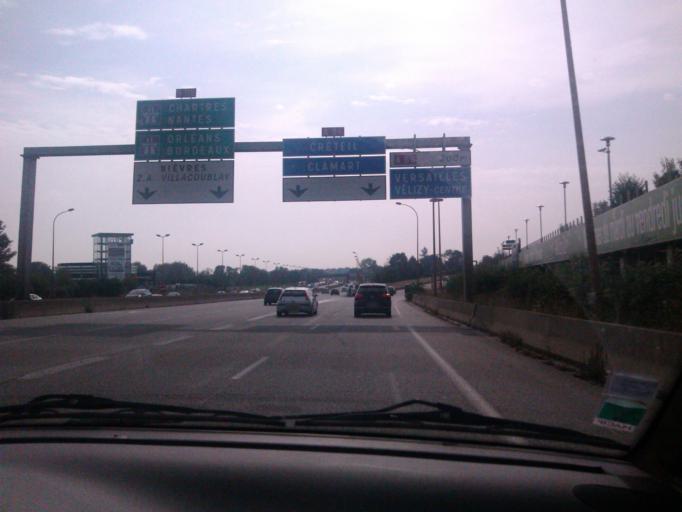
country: FR
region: Ile-de-France
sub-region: Departement de l'Essonne
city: Bievres
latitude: 48.7819
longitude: 2.2229
